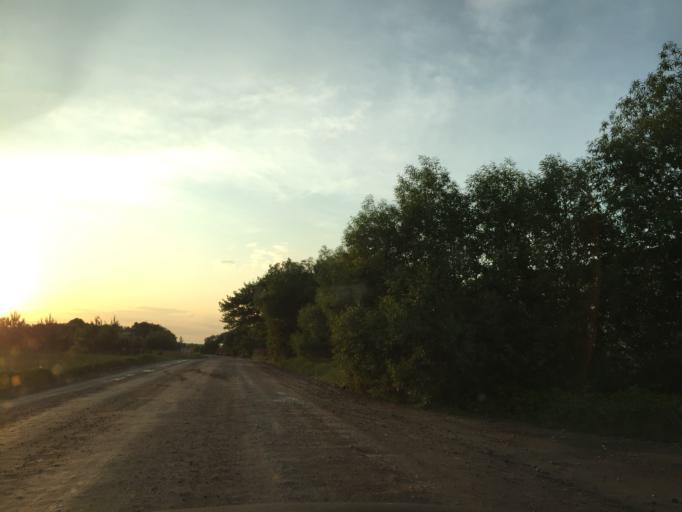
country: LT
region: Klaipedos apskritis
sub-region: Klaipeda
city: Klaipeda
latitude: 55.7544
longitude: 21.1529
